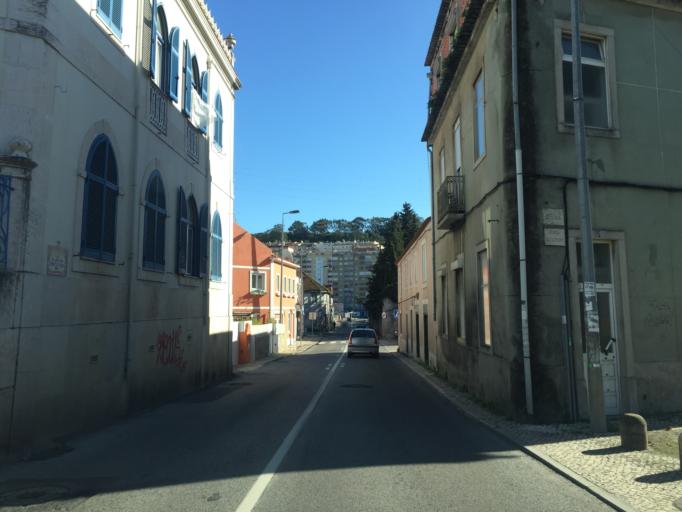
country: PT
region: Lisbon
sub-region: Sintra
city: Belas
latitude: 38.7757
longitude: -9.2636
